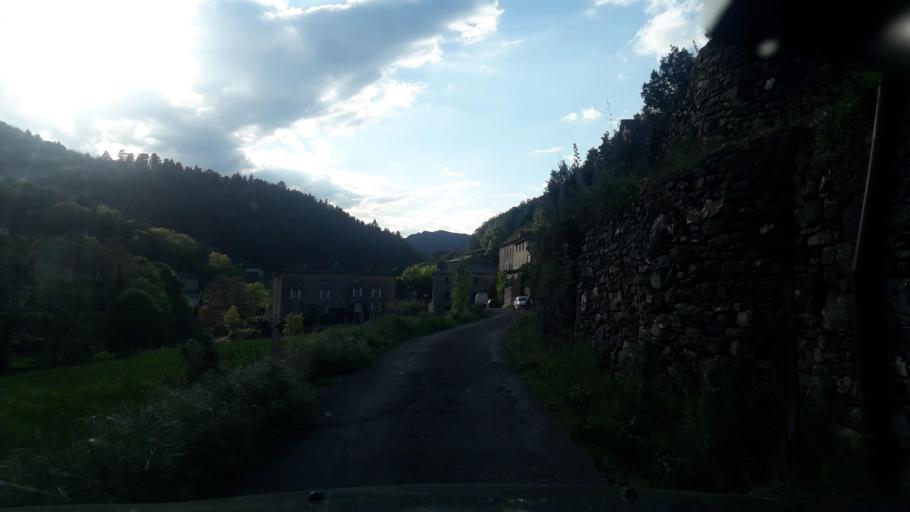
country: FR
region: Languedoc-Roussillon
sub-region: Departement du Gard
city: Valleraugue
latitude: 44.1581
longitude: 3.6808
